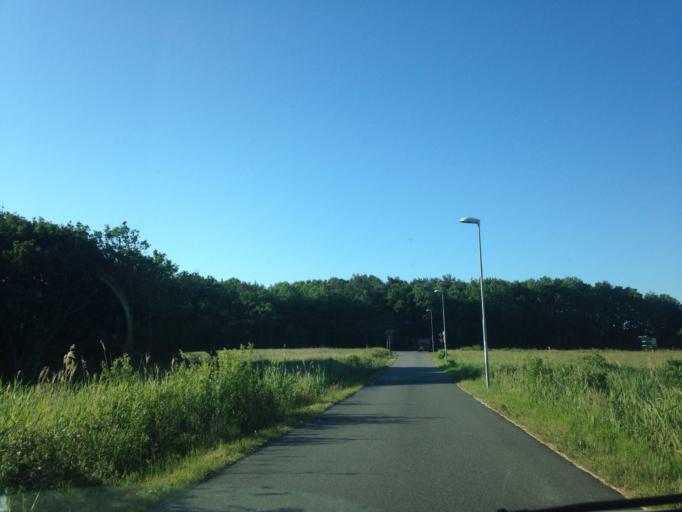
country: SE
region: Vaestra Goetaland
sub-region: Goteborg
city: Torslanda
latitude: 57.7669
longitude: 11.8405
